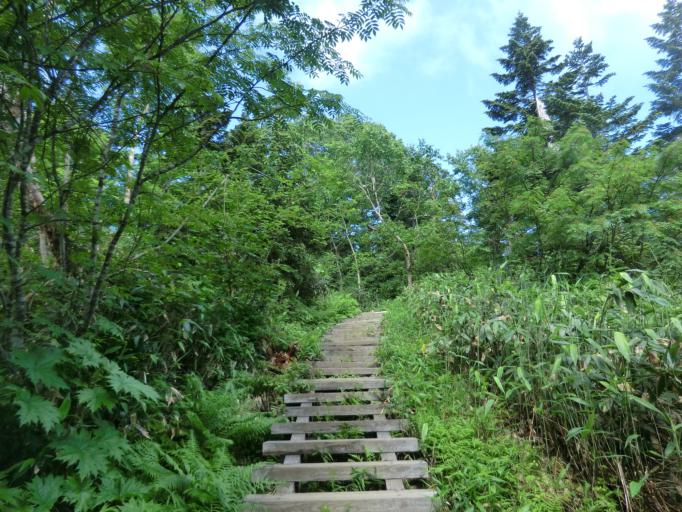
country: JP
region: Gunma
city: Numata
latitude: 36.8847
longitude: 139.1814
